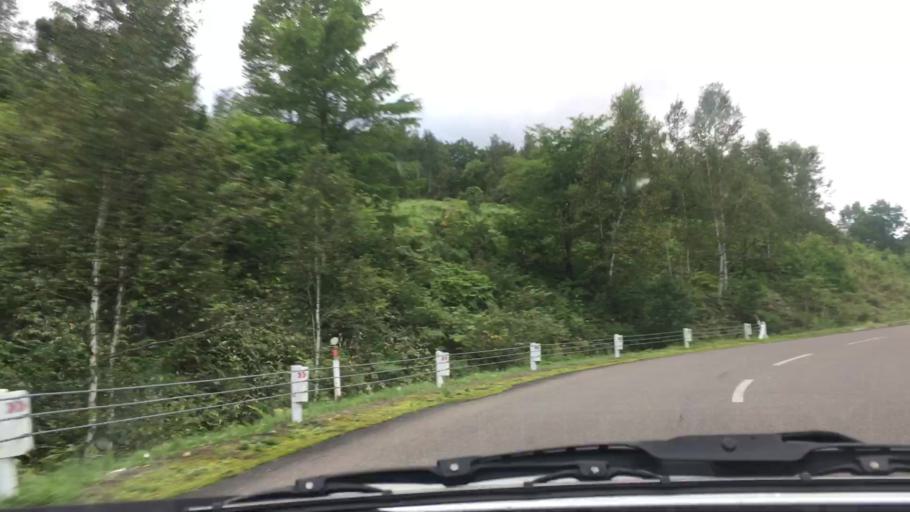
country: JP
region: Hokkaido
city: Otofuke
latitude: 43.1559
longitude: 142.8549
